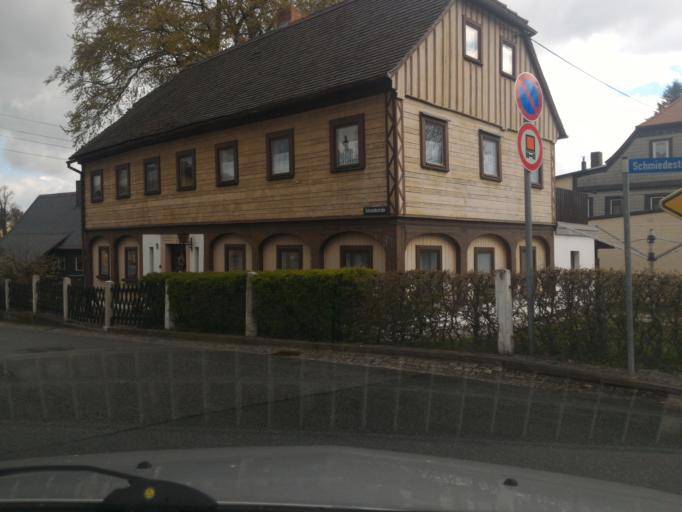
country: DE
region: Saxony
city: Grossschonau
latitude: 50.8952
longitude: 14.6697
